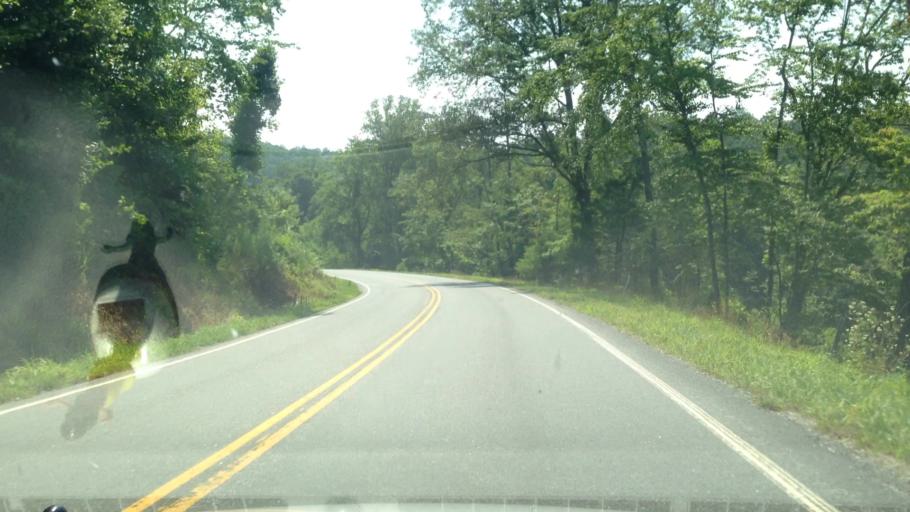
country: US
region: Virginia
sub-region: Patrick County
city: Stuart
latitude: 36.5846
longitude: -80.3884
